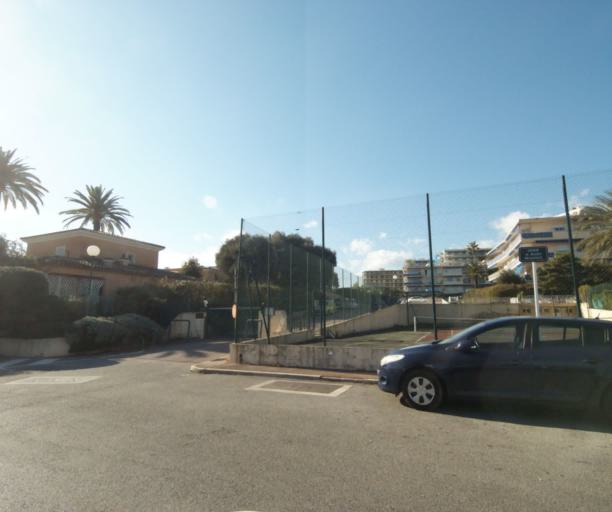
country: FR
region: Provence-Alpes-Cote d'Azur
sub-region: Departement des Alpes-Maritimes
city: Biot
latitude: 43.6082
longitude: 7.1217
